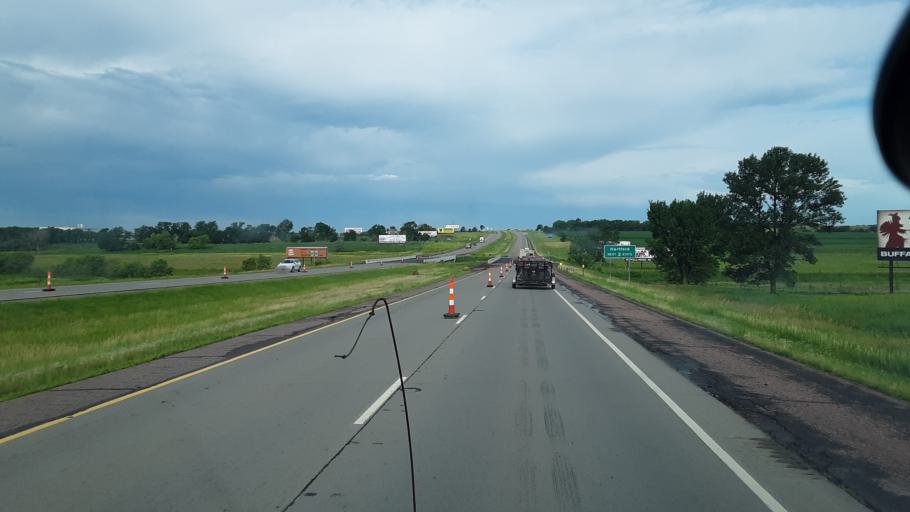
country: US
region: South Dakota
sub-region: Minnehaha County
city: Hartford
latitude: 43.6088
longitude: -96.8765
